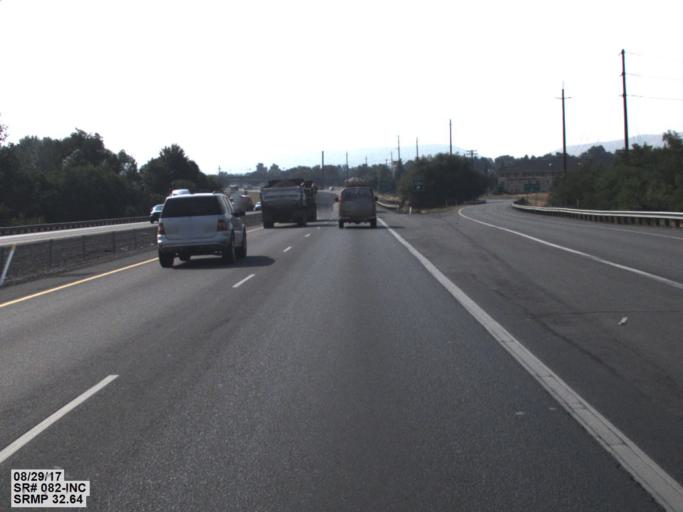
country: US
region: Washington
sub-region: Yakima County
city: Yakima
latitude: 46.6130
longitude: -120.4911
